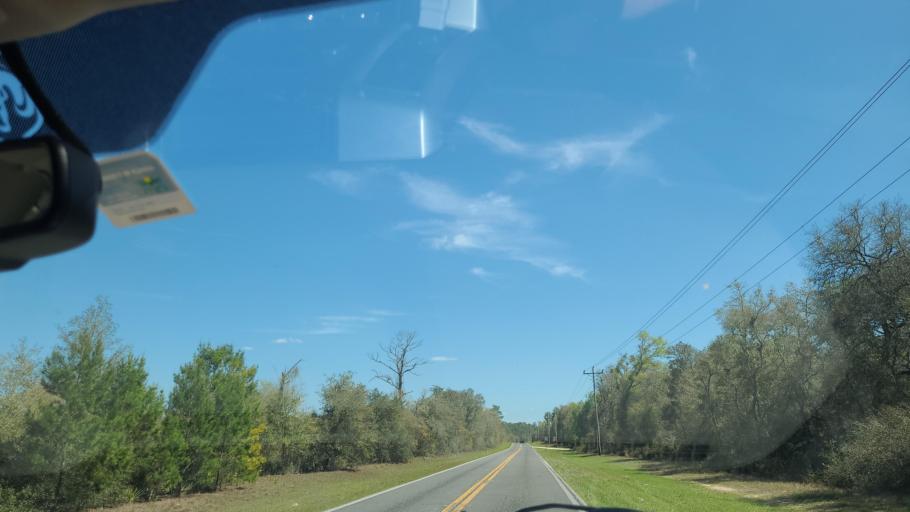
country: US
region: Florida
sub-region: Marion County
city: Citra
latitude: 29.4134
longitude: -81.9108
